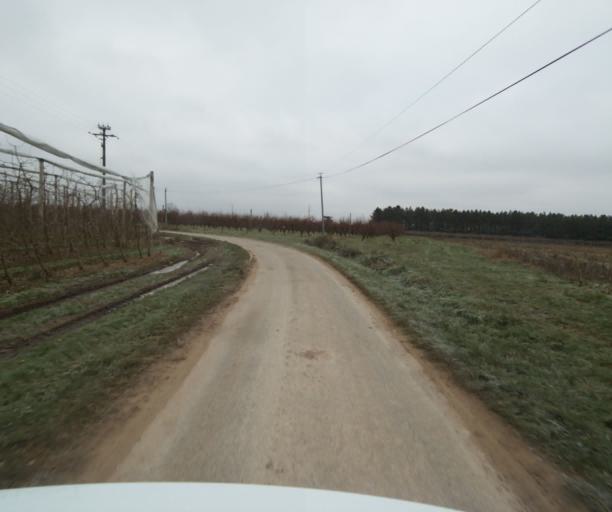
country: FR
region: Midi-Pyrenees
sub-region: Departement du Tarn-et-Garonne
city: Moissac
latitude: 44.1097
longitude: 1.1476
